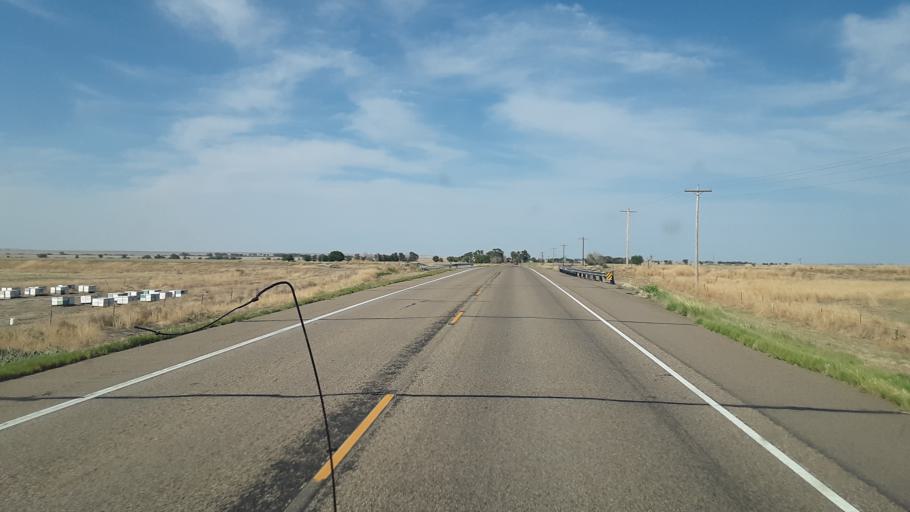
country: US
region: Colorado
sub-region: Bent County
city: Las Animas
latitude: 38.1105
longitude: -103.1029
